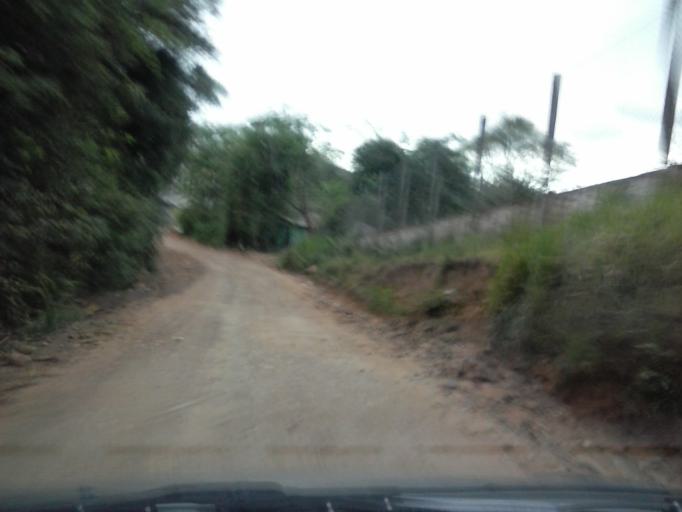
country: BR
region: Rio Grande do Sul
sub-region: Sapucaia Do Sul
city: Sapucaia
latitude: -29.8514
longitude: -51.0944
